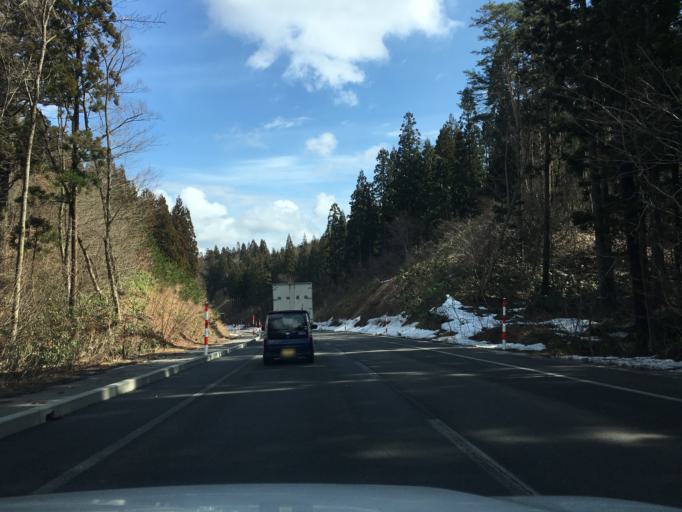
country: JP
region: Akita
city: Takanosu
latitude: 40.1111
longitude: 140.3649
